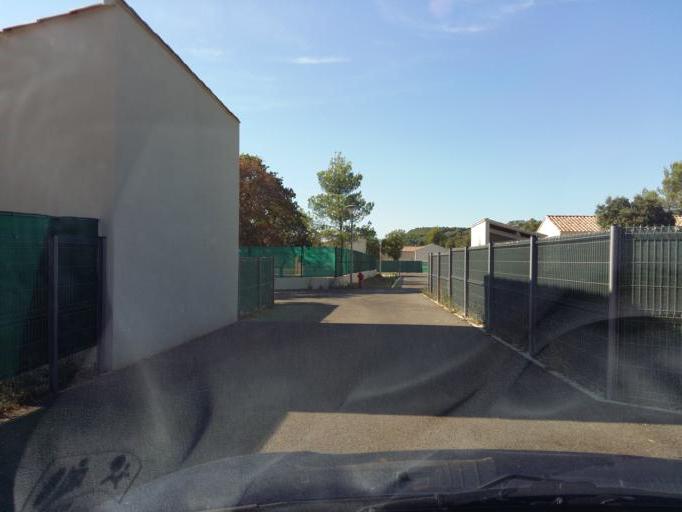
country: FR
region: Provence-Alpes-Cote d'Azur
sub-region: Departement du Vaucluse
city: Saint-Didier
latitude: 44.0207
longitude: 5.0990
